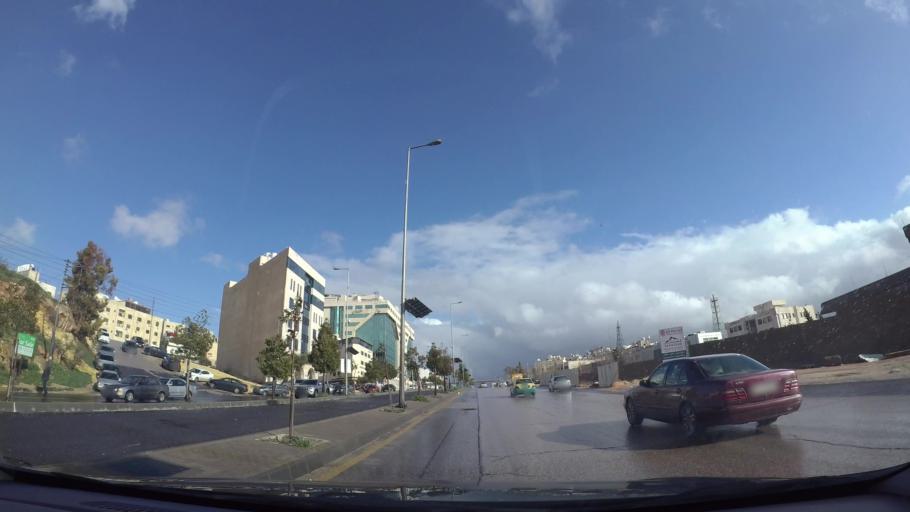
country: JO
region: Amman
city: Al Jubayhah
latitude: 31.9995
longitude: 35.8792
